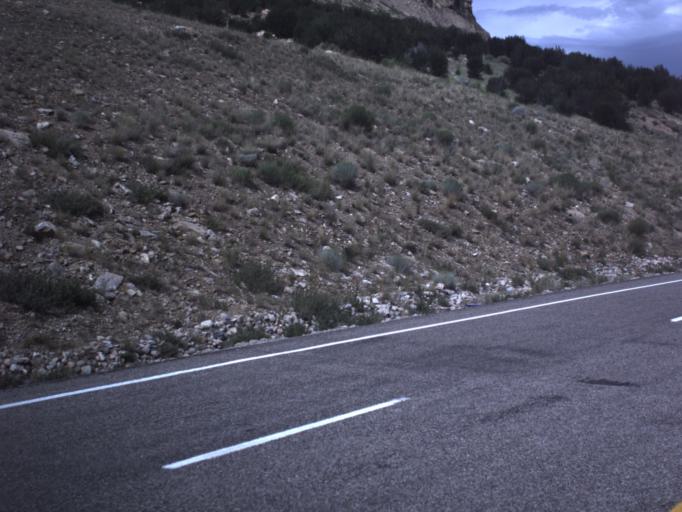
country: US
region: Utah
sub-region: Iron County
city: Cedar City
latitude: 37.6325
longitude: -112.9419
